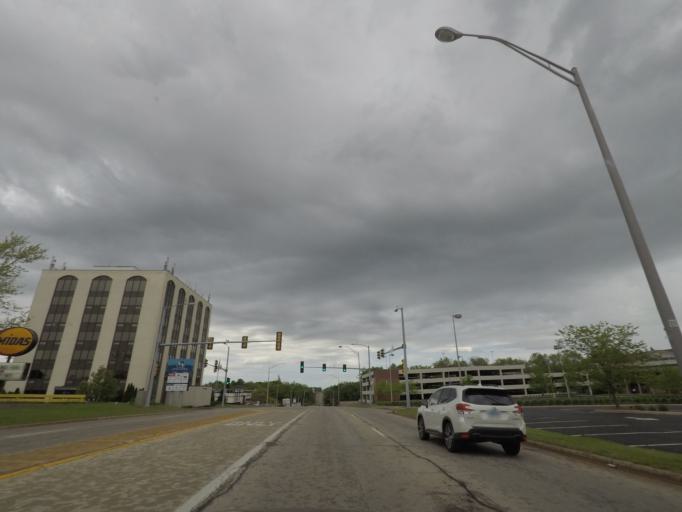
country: US
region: Illinois
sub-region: Winnebago County
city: Rockford
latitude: 42.2550
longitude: -89.0290
